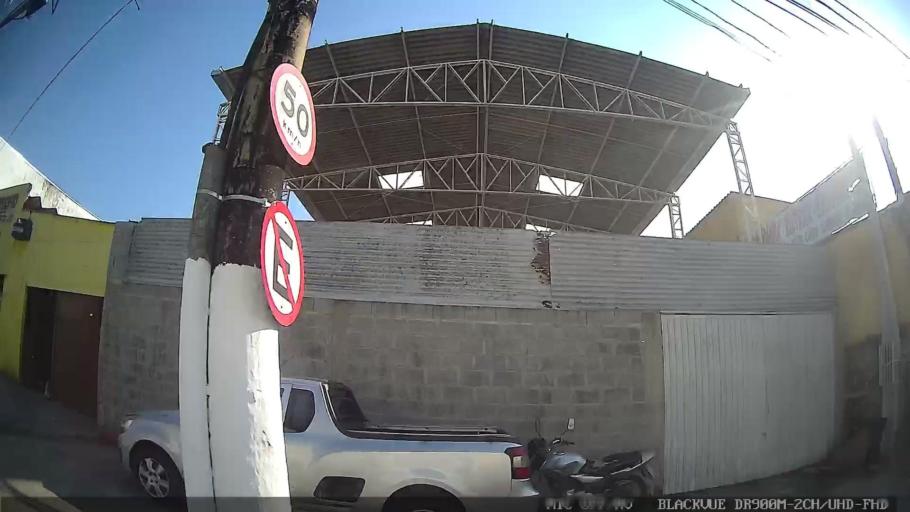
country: BR
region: Sao Paulo
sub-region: Guaruja
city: Guaruja
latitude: -23.9908
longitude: -46.2671
